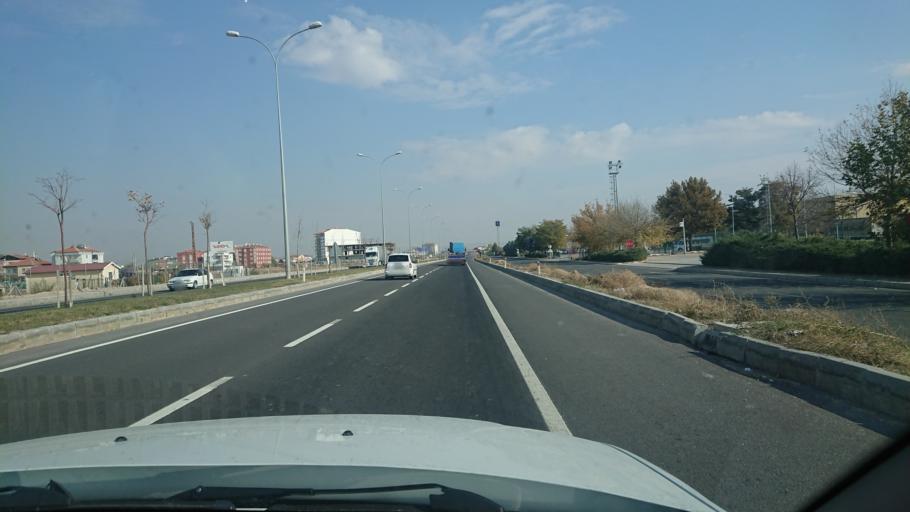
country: TR
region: Aksaray
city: Aksaray
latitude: 38.3511
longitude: 33.9636
